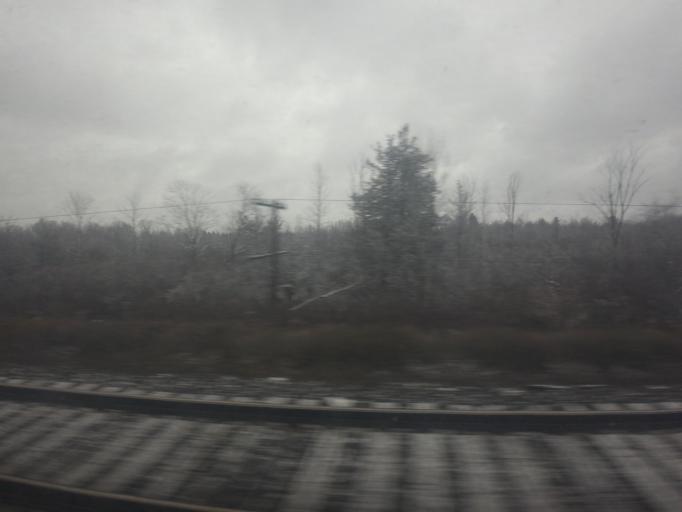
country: US
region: New York
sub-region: Jefferson County
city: Alexandria Bay
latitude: 44.4203
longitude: -75.9889
